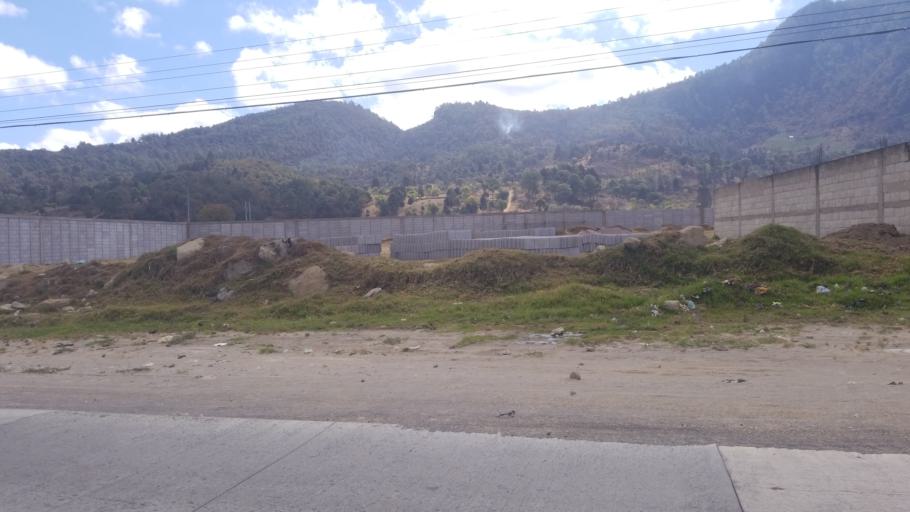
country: GT
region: Quetzaltenango
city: Quetzaltenango
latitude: 14.8113
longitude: -91.5395
